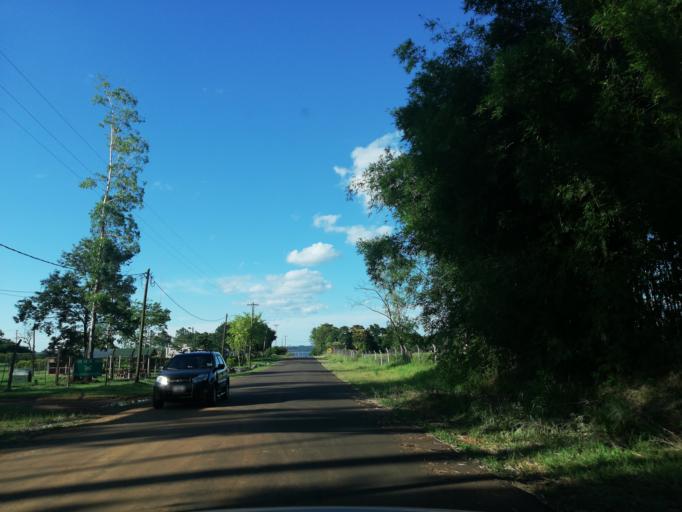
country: AR
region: Misiones
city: Garupa
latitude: -27.4619
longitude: -55.7972
